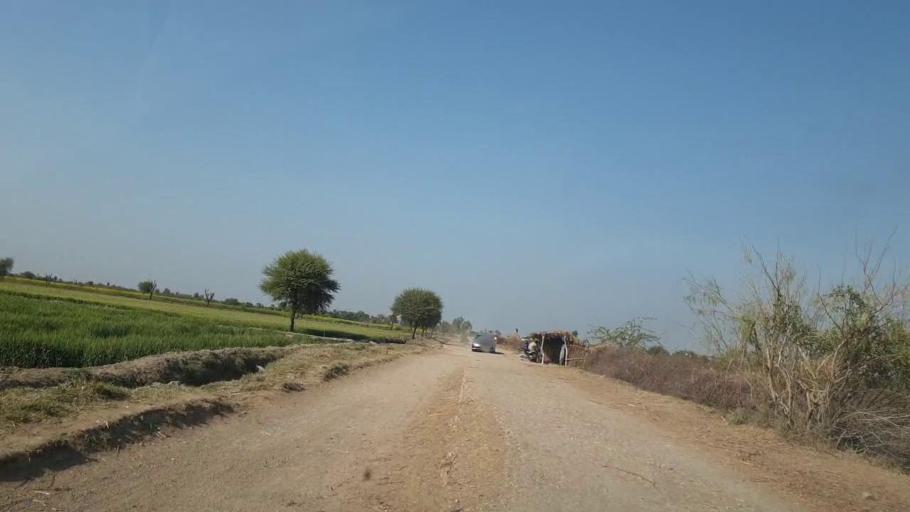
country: PK
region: Sindh
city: Tando Mittha Khan
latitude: 25.7630
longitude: 69.1937
